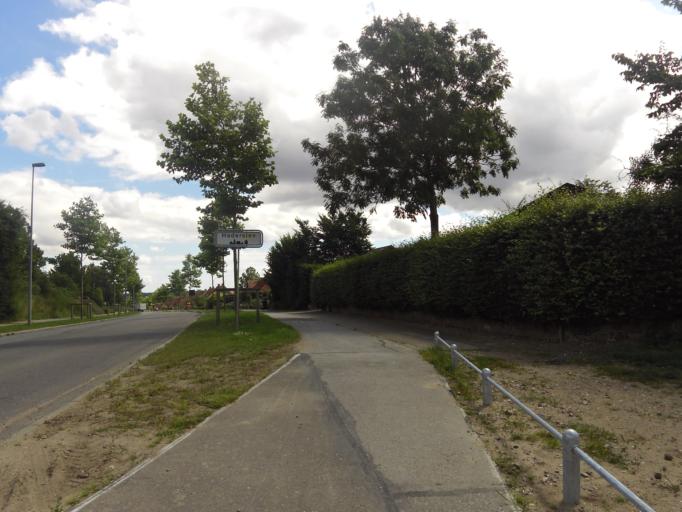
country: DK
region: South Denmark
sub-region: Haderslev Kommune
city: Haderslev
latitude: 55.2529
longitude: 9.4570
